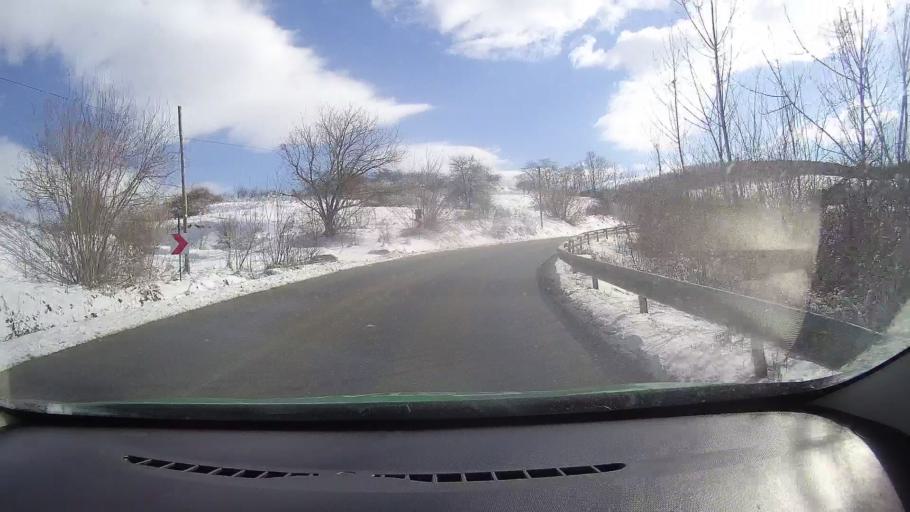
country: RO
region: Sibiu
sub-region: Comuna Barghis
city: Barghis
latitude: 45.9820
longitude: 24.5103
